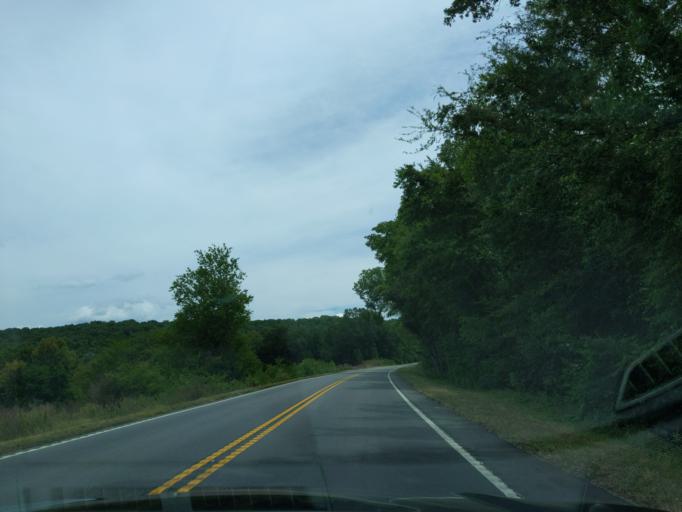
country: US
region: North Carolina
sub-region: Cabarrus County
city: Mount Pleasant
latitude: 35.4374
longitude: -80.3912
